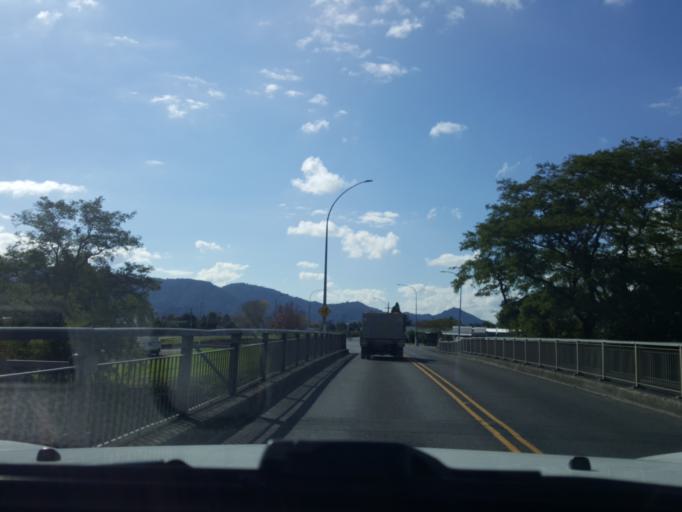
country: NZ
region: Waikato
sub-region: Waikato District
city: Ngaruawahia
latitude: -37.6625
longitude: 175.1492
